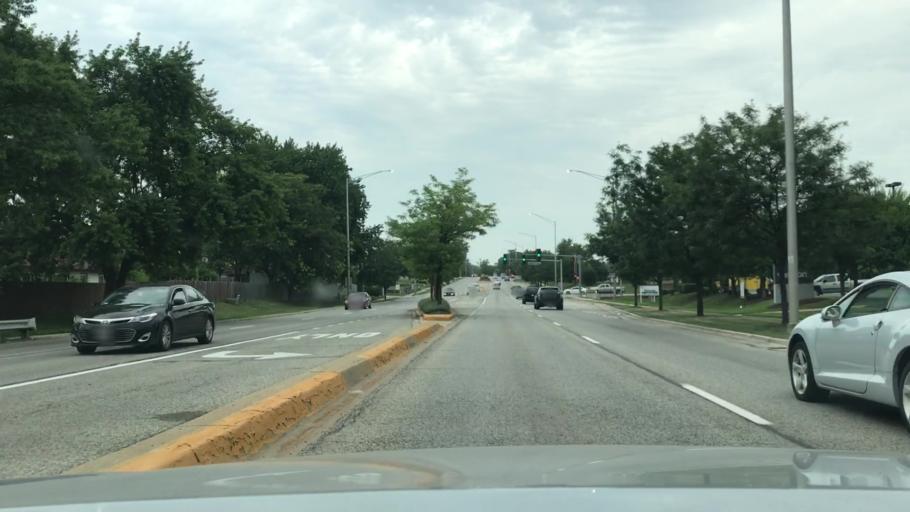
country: US
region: Illinois
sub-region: Will County
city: Bolingbrook
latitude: 41.7005
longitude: -88.0683
